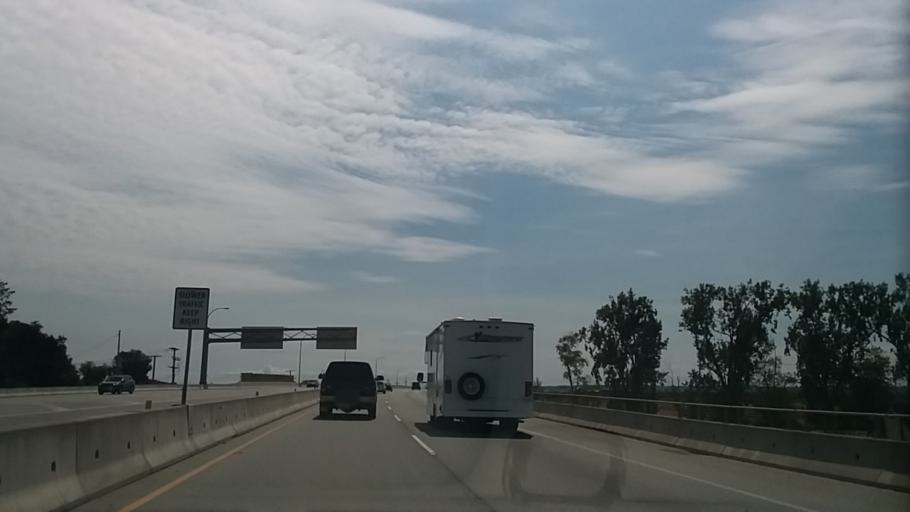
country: CA
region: British Columbia
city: Ladner
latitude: 49.0913
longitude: -123.0250
